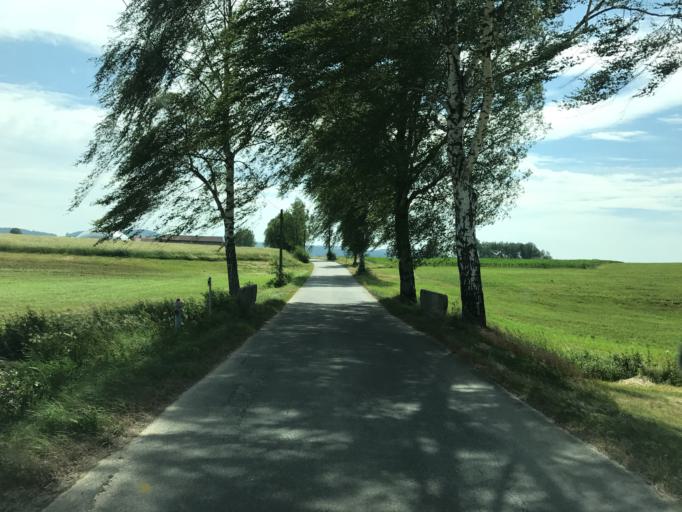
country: DE
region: Bavaria
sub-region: Upper Palatinate
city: Schonthal
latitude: 49.3477
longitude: 12.6381
